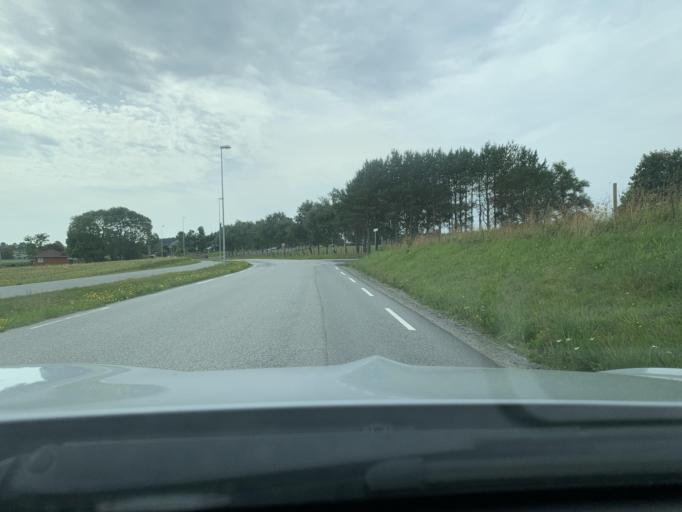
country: NO
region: Rogaland
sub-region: Time
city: Bryne
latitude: 58.7616
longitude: 5.7103
